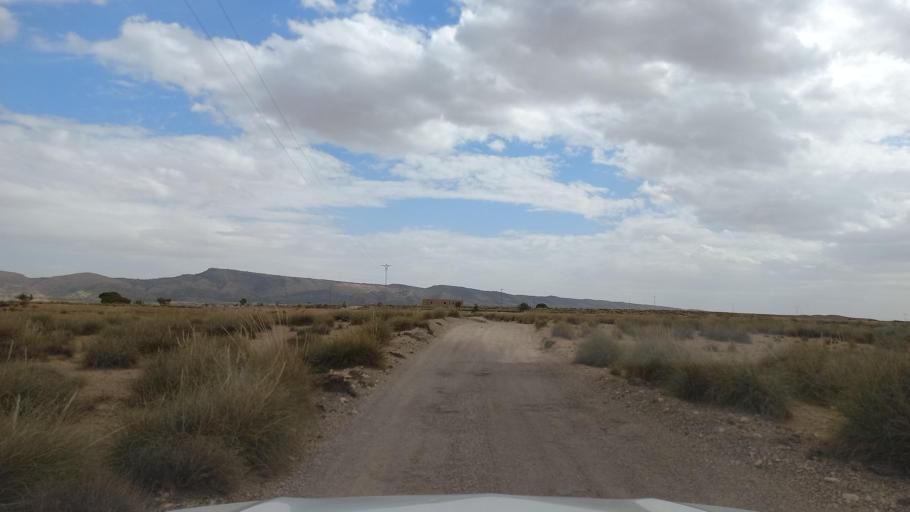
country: TN
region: Al Qasrayn
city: Sbiba
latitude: 35.3823
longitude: 9.1152
